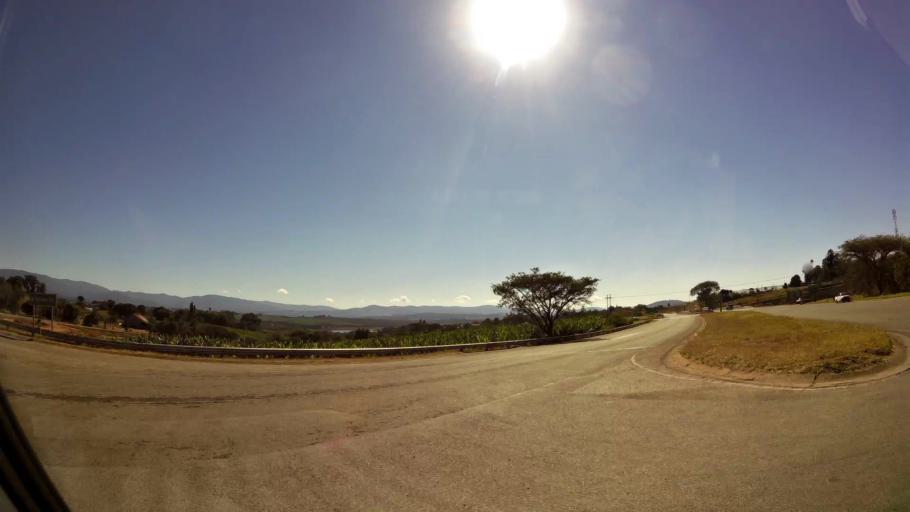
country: ZA
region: Limpopo
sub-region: Mopani District Municipality
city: Tzaneen
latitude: -23.8373
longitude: 30.1345
